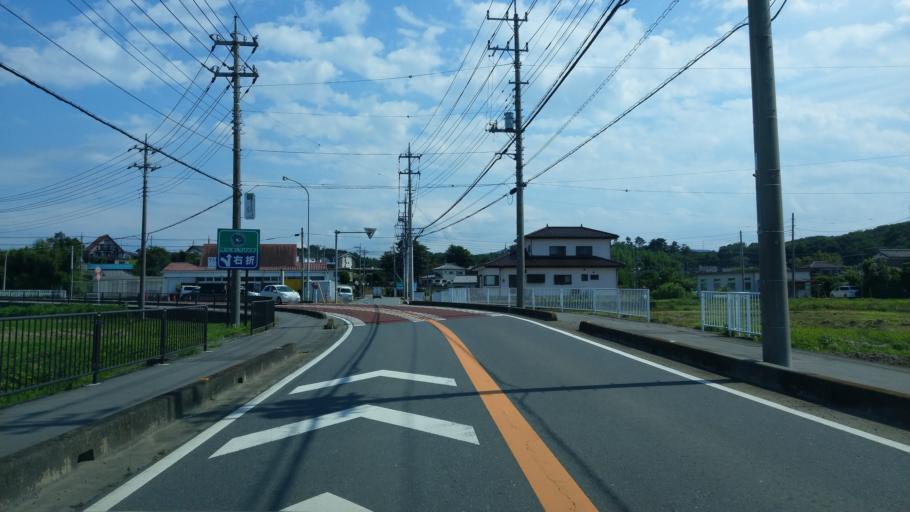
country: JP
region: Saitama
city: Kodamacho-kodamaminami
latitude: 36.2059
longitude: 139.1517
